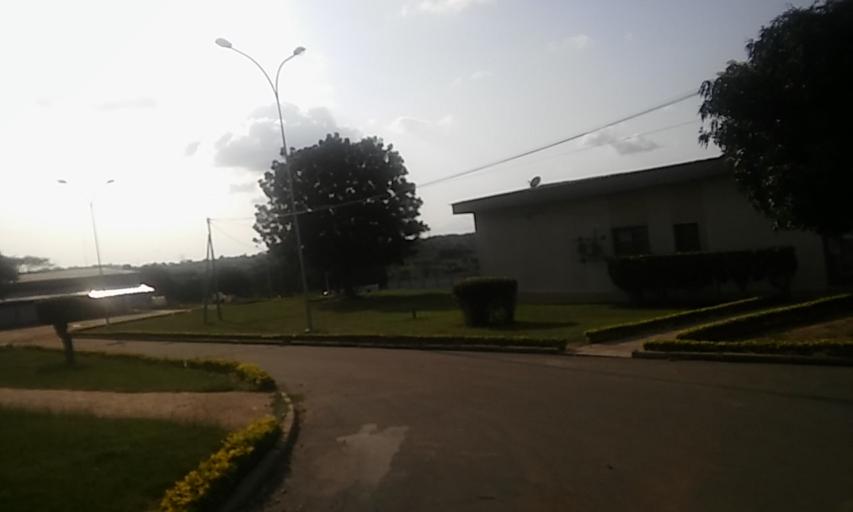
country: CI
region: Vallee du Bandama
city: Bouake
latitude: 7.6880
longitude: -5.0655
